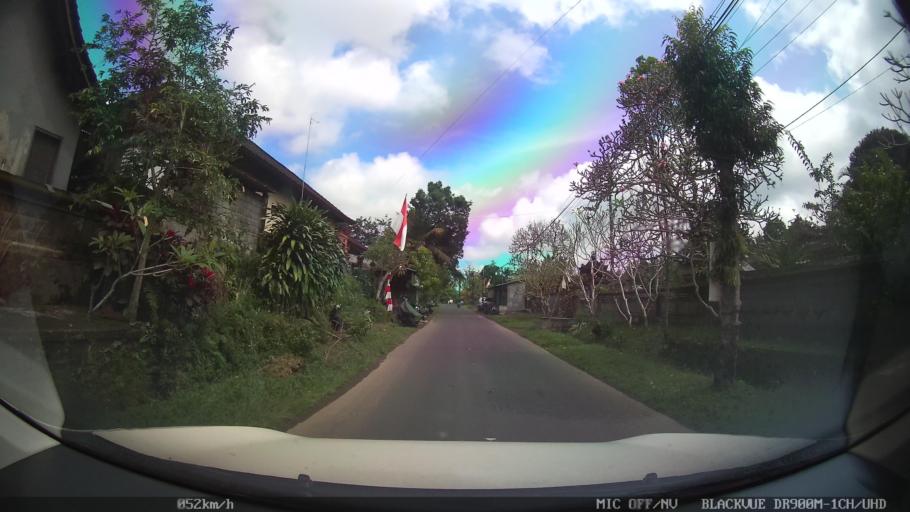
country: ID
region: Bali
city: Banjar Mulung
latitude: -8.4971
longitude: 115.3204
